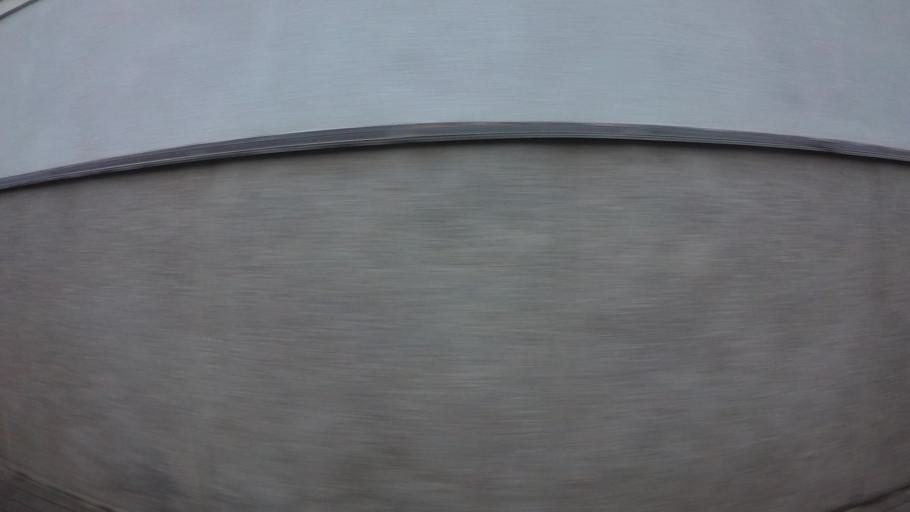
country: BA
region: Federation of Bosnia and Herzegovina
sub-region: Hercegovacko-Bosanski Kanton
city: Mostar
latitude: 43.3377
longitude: 17.8039
